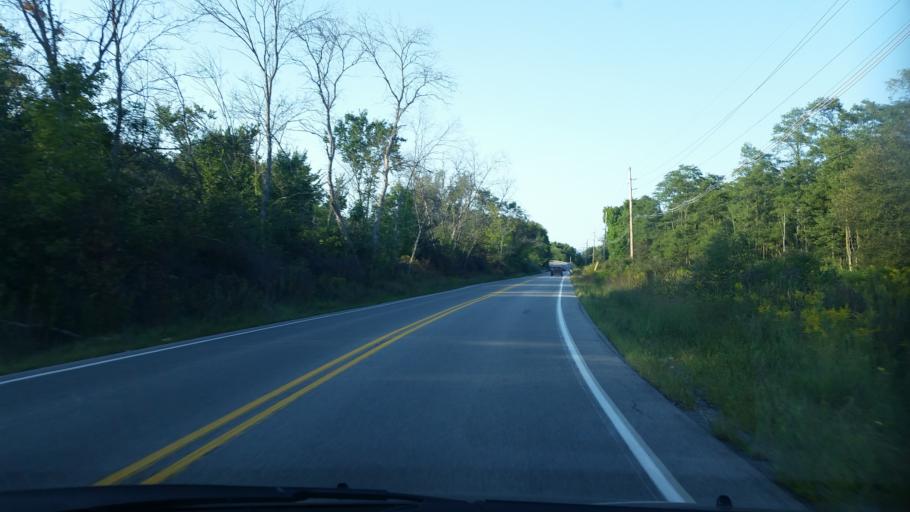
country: US
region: Pennsylvania
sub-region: Blair County
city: Greenwood
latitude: 40.5715
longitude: -78.3537
